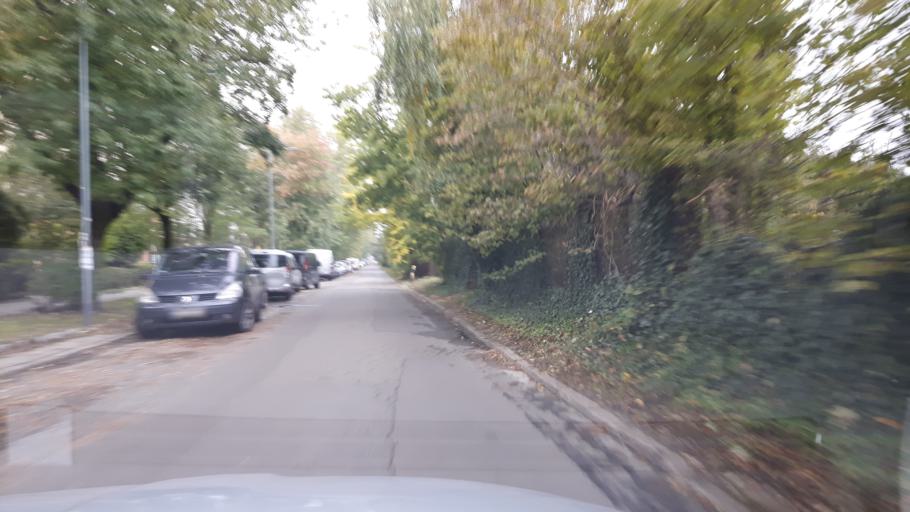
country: PL
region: Masovian Voivodeship
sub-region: Warszawa
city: Praga Poludnie
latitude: 52.2506
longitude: 21.0987
